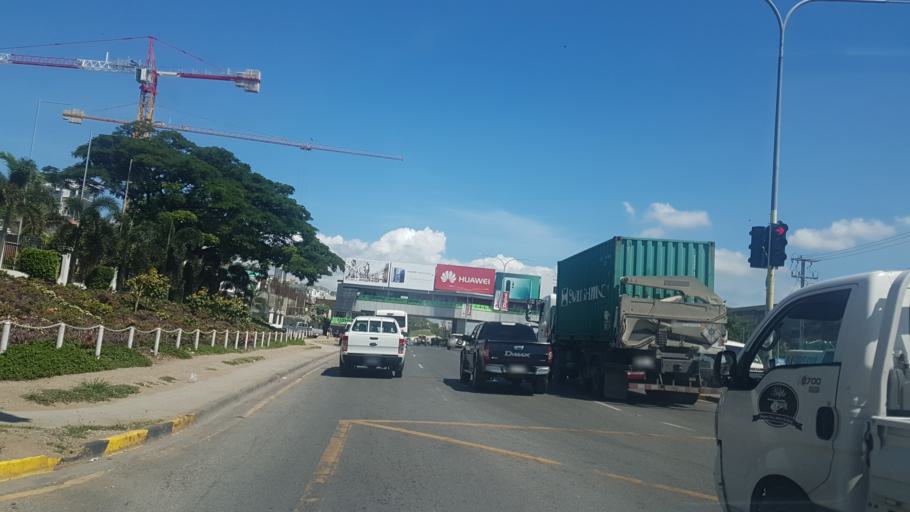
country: PG
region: National Capital
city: Port Moresby
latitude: -9.4399
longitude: 147.1805
